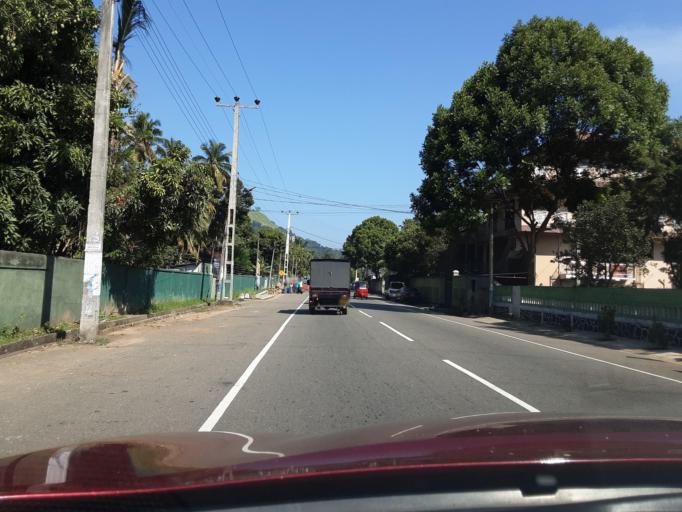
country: LK
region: Uva
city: Badulla
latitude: 6.9954
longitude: 81.0576
